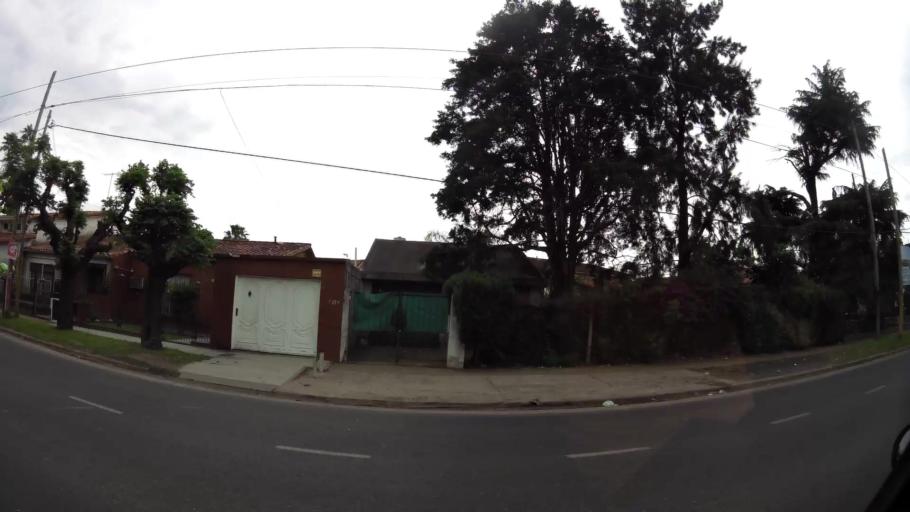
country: AR
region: Buenos Aires
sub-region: Partido de Quilmes
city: Quilmes
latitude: -34.7525
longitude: -58.2900
